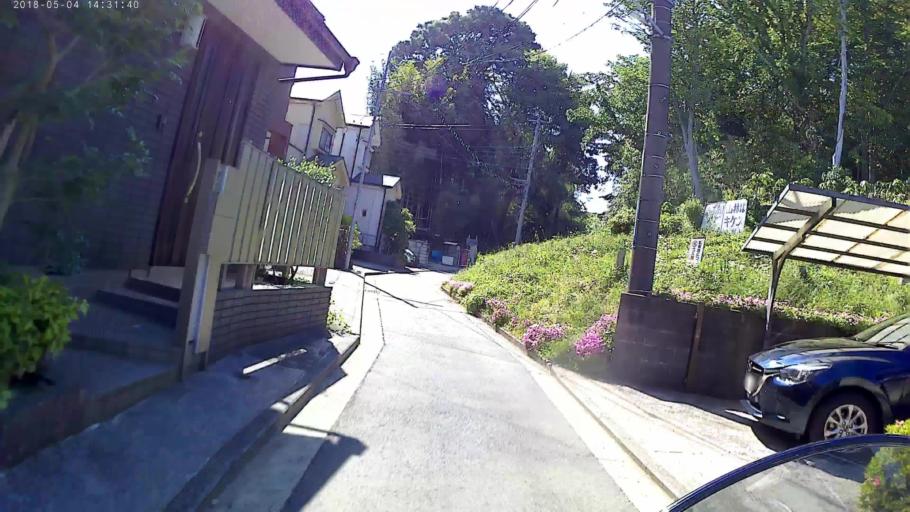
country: JP
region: Kanagawa
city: Yokohama
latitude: 35.4889
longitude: 139.6026
